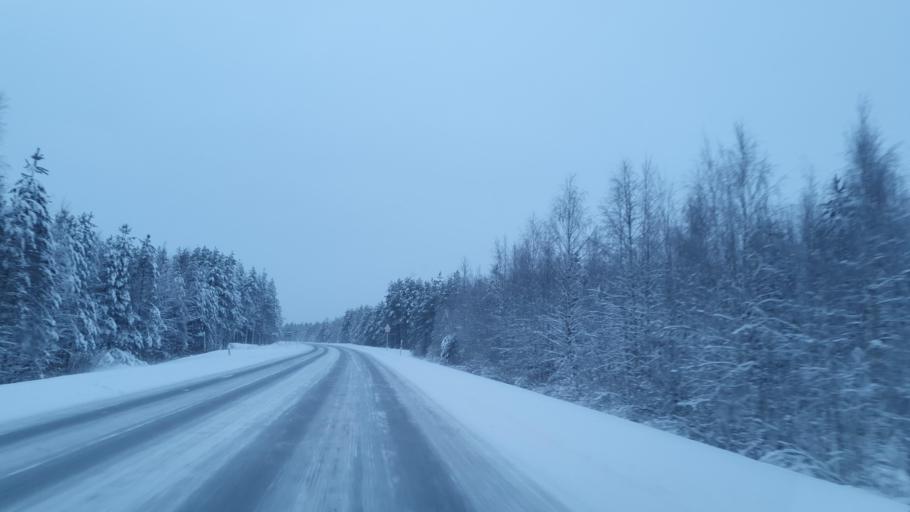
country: FI
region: Kainuu
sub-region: Kajaani
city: Vaala
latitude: 64.5964
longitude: 26.7798
